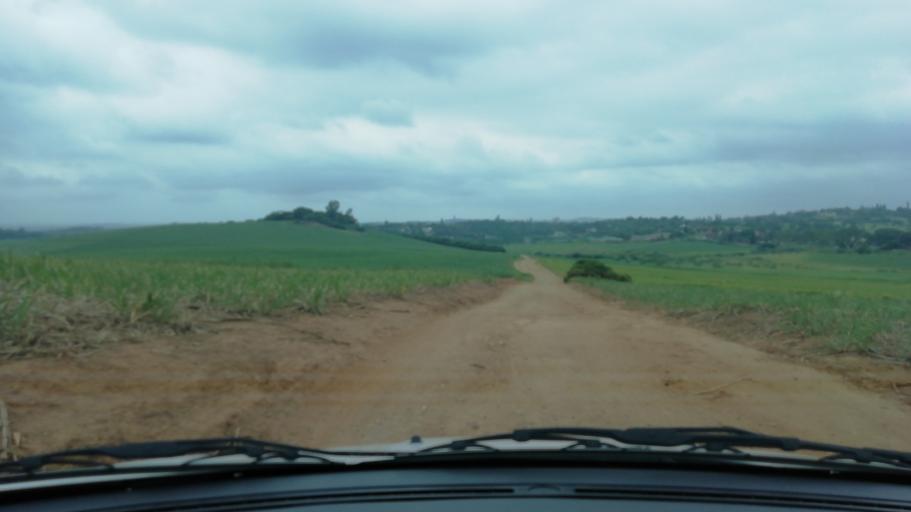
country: ZA
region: KwaZulu-Natal
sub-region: uThungulu District Municipality
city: Empangeni
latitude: -28.7317
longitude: 31.9081
